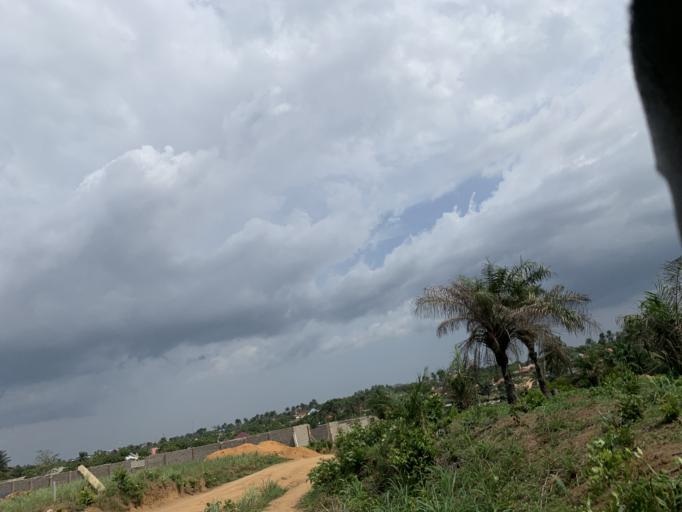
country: SL
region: Western Area
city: Waterloo
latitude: 8.3528
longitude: -13.0492
